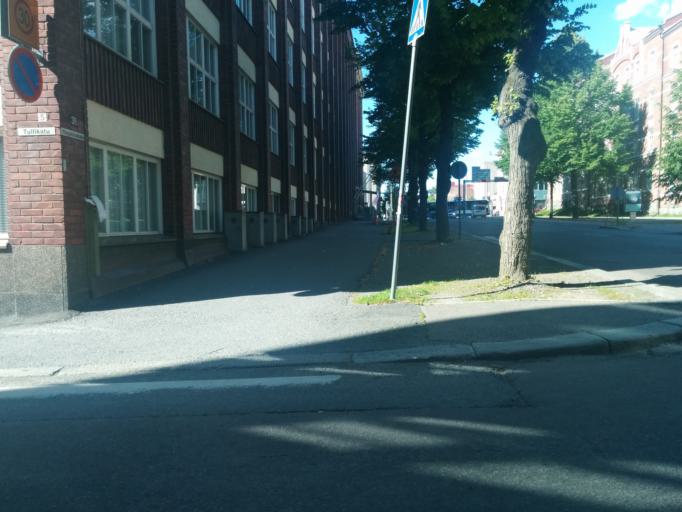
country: FI
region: Pirkanmaa
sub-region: Tampere
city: Tampere
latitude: 61.4979
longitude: 23.7796
